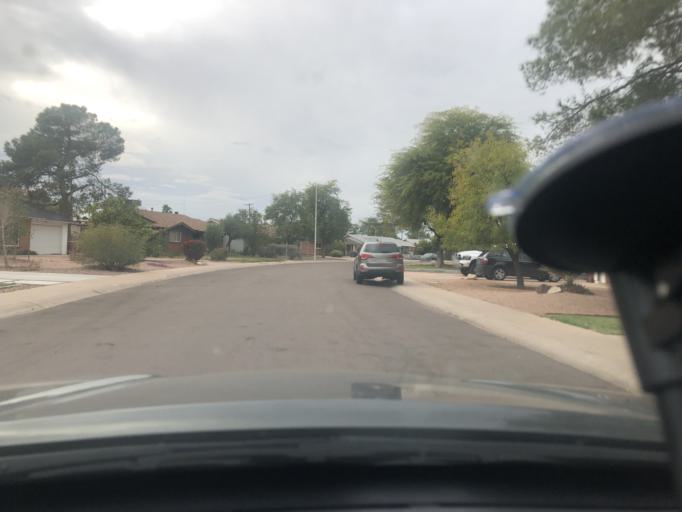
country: US
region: Arizona
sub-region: Maricopa County
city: Scottsdale
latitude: 33.4823
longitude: -111.8970
